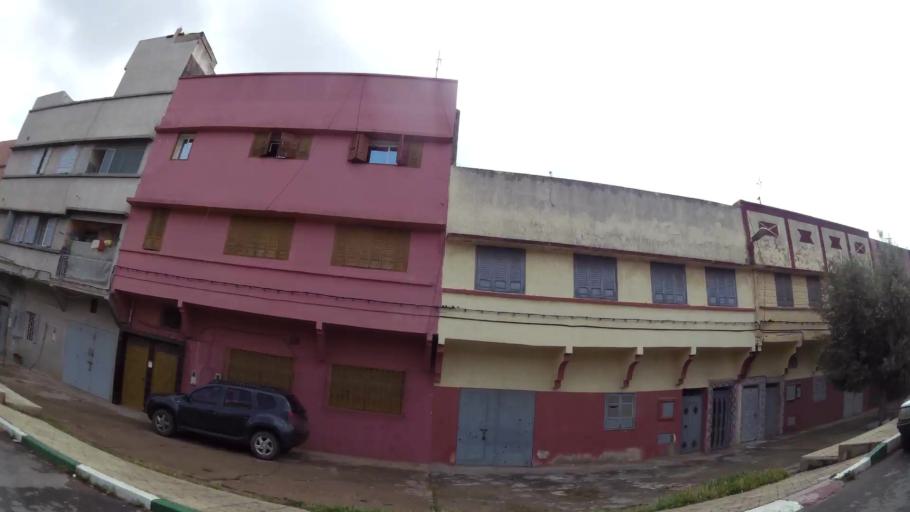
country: MA
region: Rabat-Sale-Zemmour-Zaer
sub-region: Khemisset
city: Tiflet
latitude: 33.8966
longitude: -6.3096
